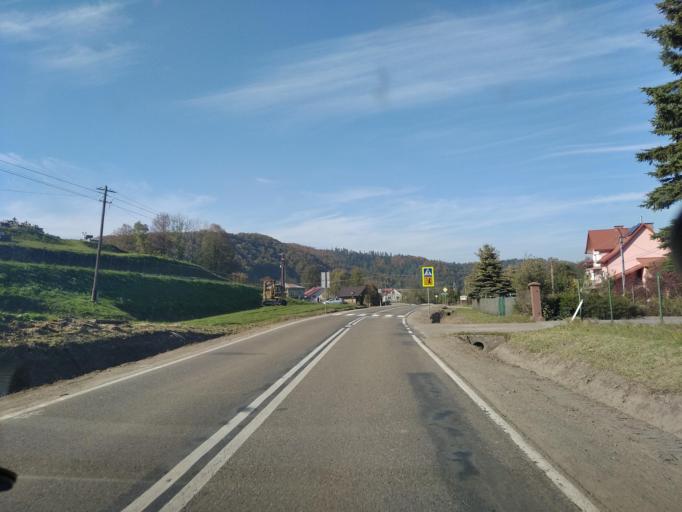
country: PL
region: Subcarpathian Voivodeship
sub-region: Powiat leski
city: Baligrod
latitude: 49.3898
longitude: 22.2858
